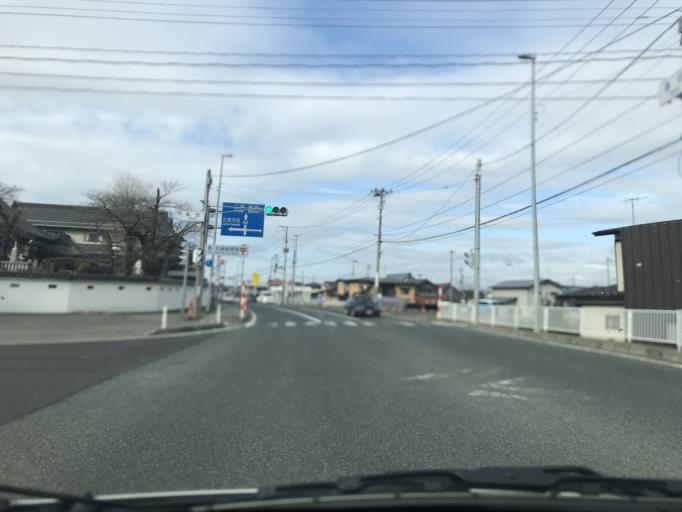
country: JP
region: Iwate
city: Hanamaki
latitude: 39.3856
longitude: 141.1251
